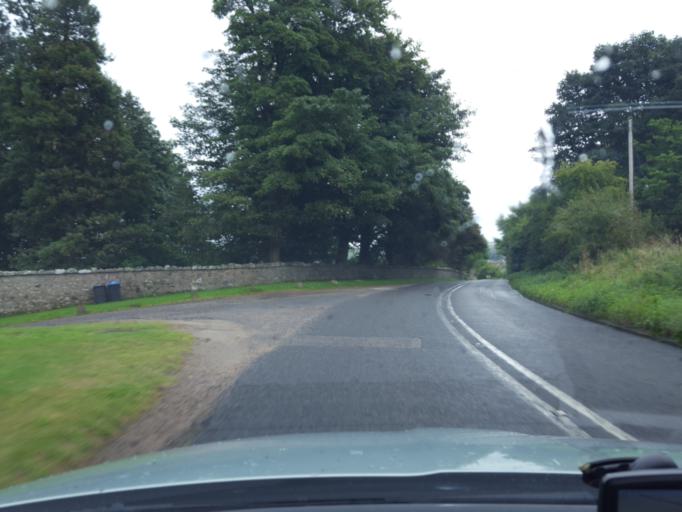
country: GB
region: Scotland
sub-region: Aberdeenshire
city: Stonehaven
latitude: 56.9789
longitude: -2.2437
